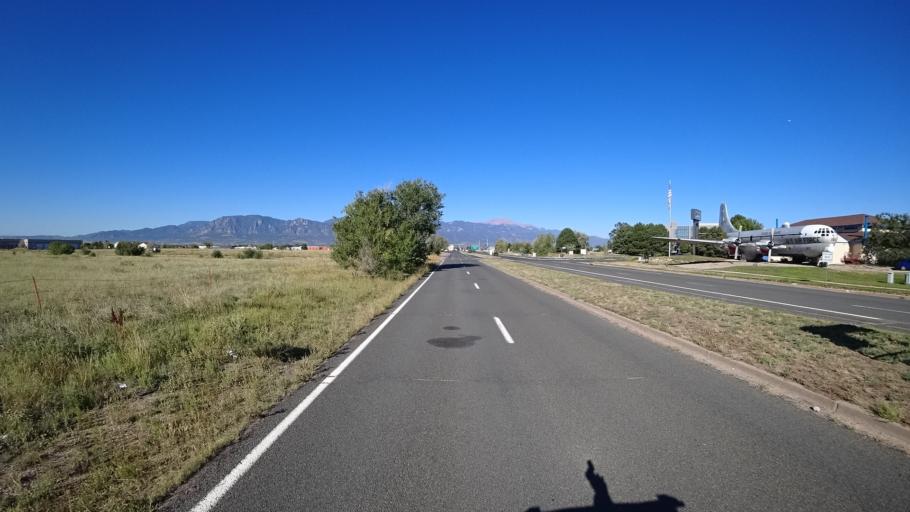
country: US
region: Colorado
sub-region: El Paso County
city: Cimarron Hills
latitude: 38.8061
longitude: -104.7259
